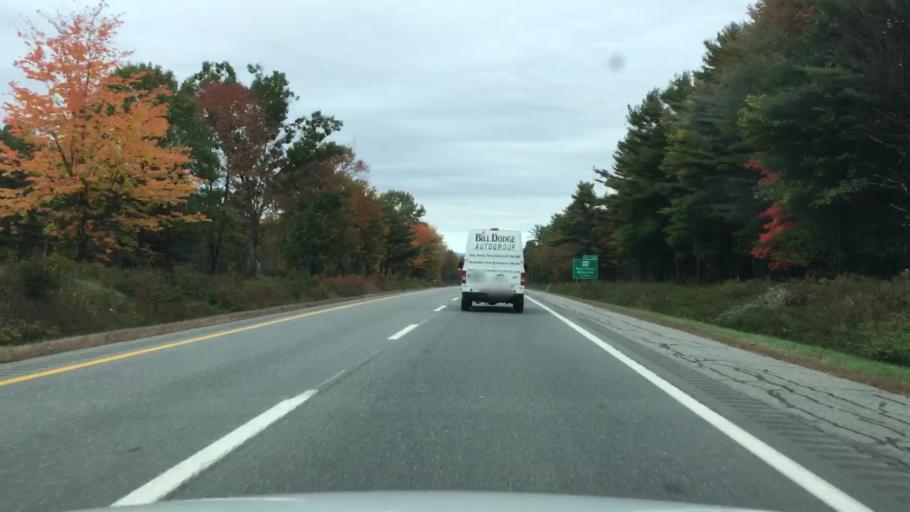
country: US
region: Maine
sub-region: Kennebec County
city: Waterville
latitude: 44.5590
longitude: -69.6731
